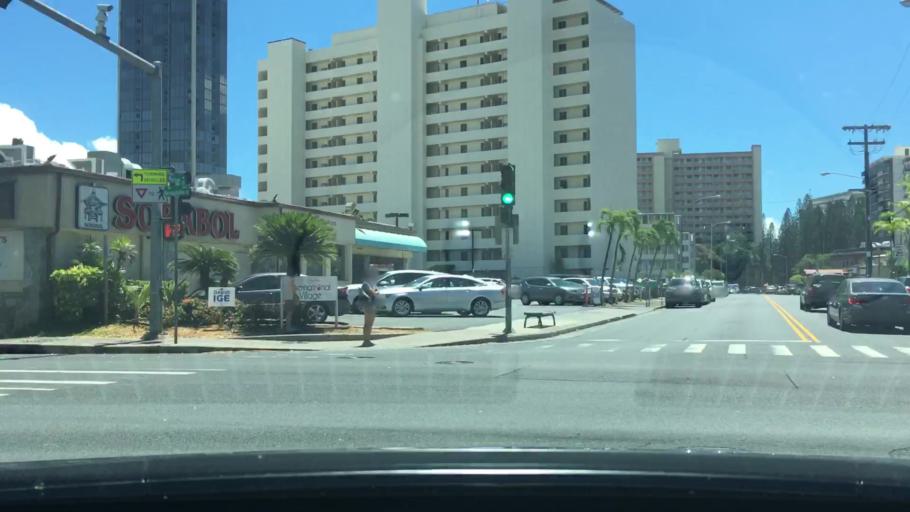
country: US
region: Hawaii
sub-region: Honolulu County
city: Honolulu
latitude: 21.2962
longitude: -157.8413
